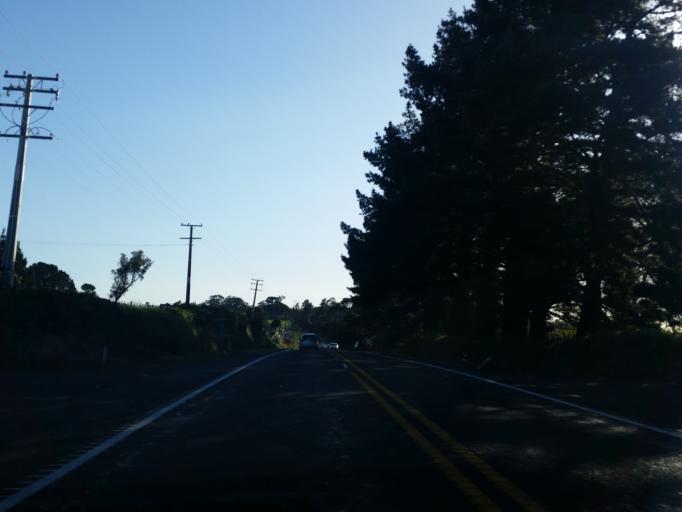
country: NZ
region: Bay of Plenty
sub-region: Western Bay of Plenty District
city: Waihi Beach
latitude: -37.4697
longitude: 175.9357
